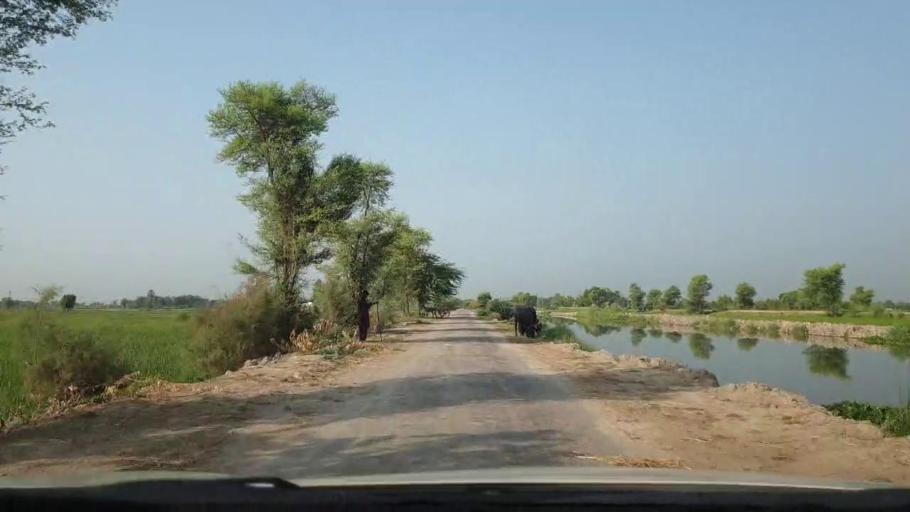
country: PK
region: Sindh
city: Larkana
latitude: 27.4918
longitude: 68.1675
